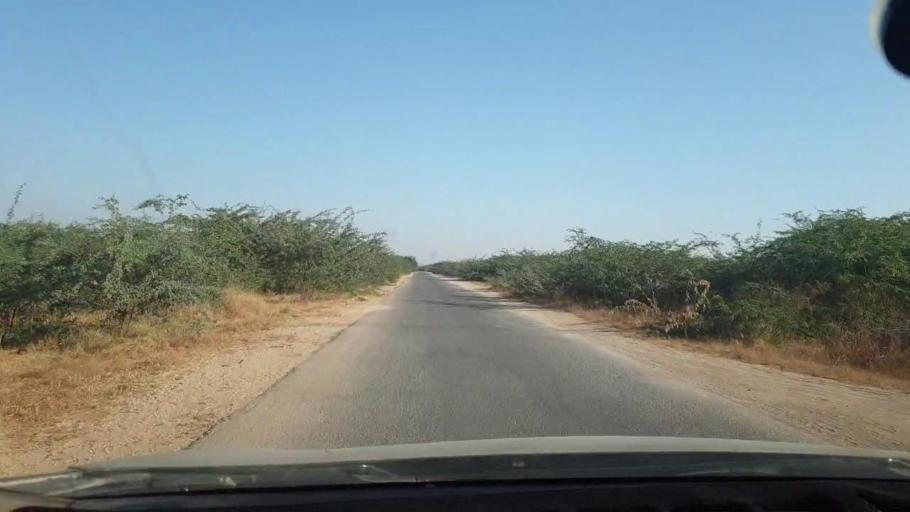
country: PK
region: Sindh
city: Malir Cantonment
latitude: 25.1622
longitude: 67.1949
